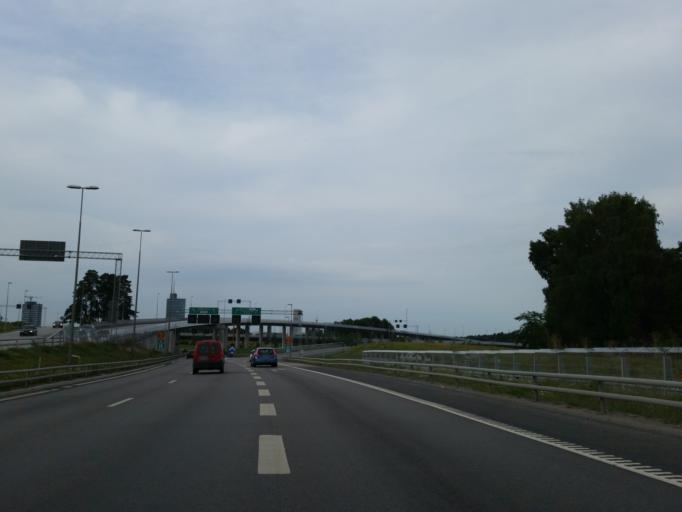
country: SE
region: Stockholm
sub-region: Stockholms Kommun
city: Kista
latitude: 59.3856
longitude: 17.9391
